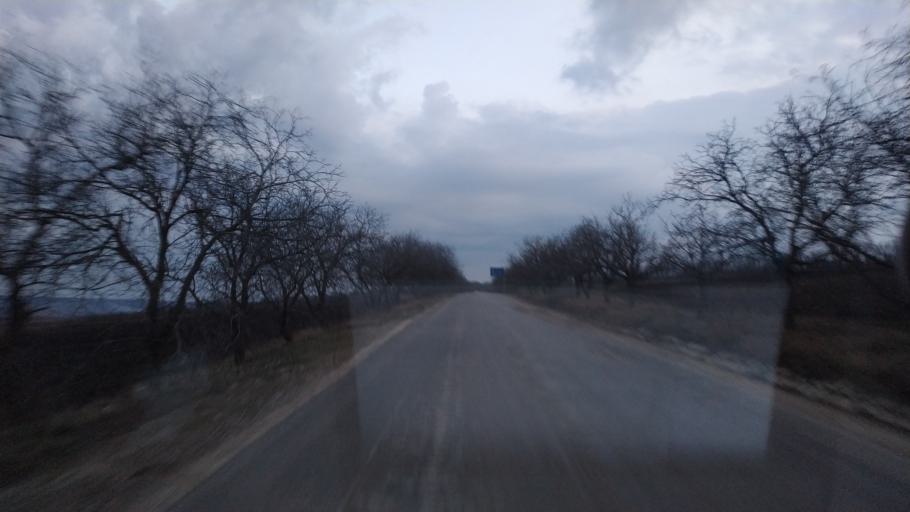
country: MD
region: Anenii Noi
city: Anenii Noi
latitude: 46.9358
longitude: 29.2858
